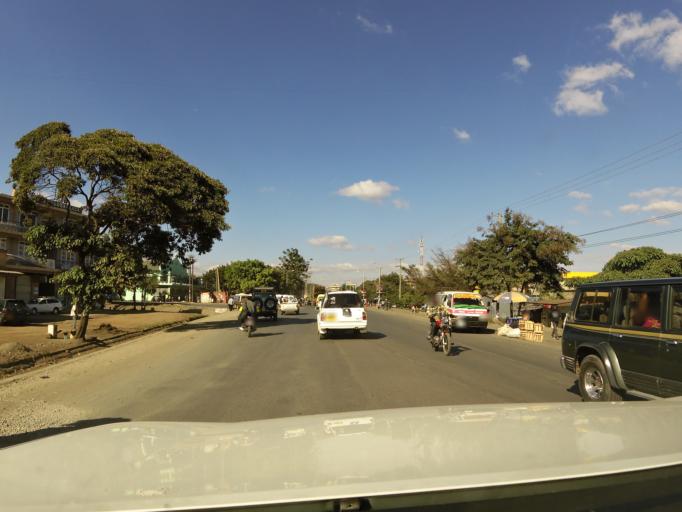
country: TZ
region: Arusha
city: Arusha
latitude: -3.3754
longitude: 36.6737
